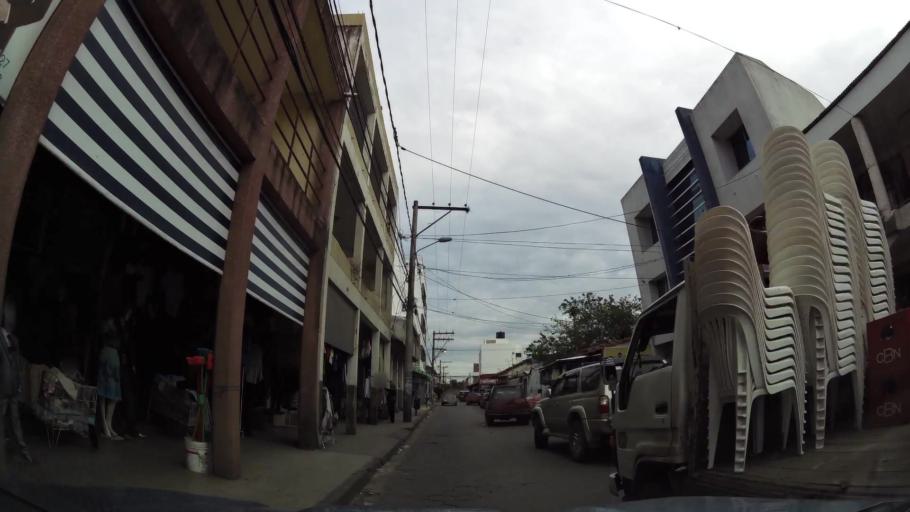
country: BO
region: Santa Cruz
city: Santa Cruz de la Sierra
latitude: -17.7807
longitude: -63.1767
